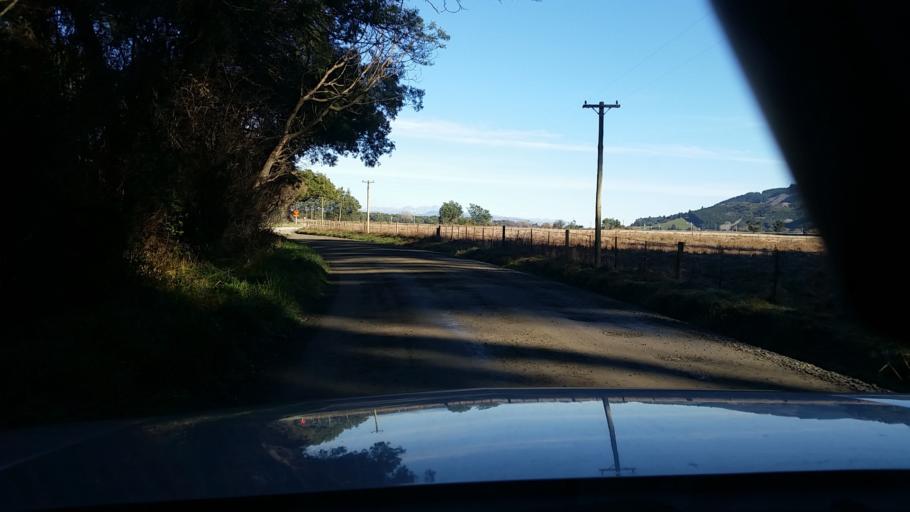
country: NZ
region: Marlborough
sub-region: Marlborough District
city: Blenheim
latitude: -41.4503
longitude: 173.8731
